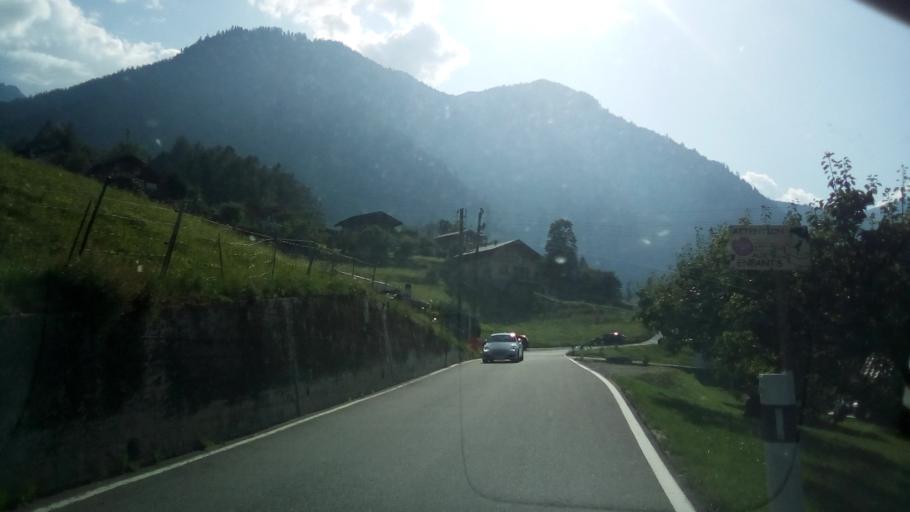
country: CH
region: Valais
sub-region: Martigny District
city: Martigny-Combe
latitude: 46.0704
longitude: 7.0768
